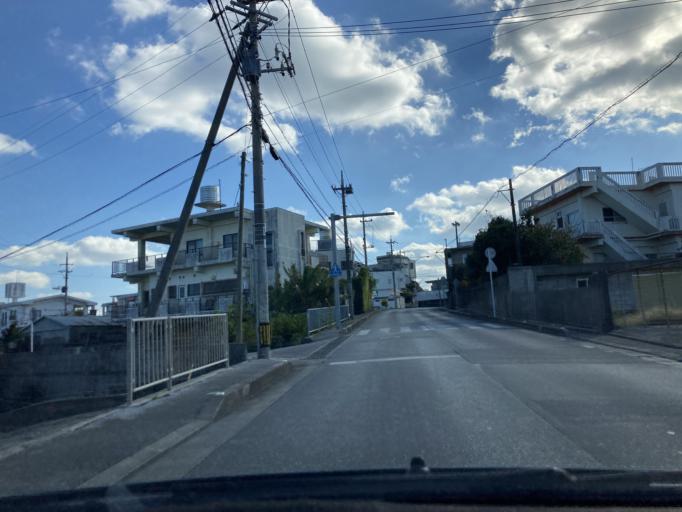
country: JP
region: Okinawa
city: Katsuren-haebaru
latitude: 26.3100
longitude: 127.9122
